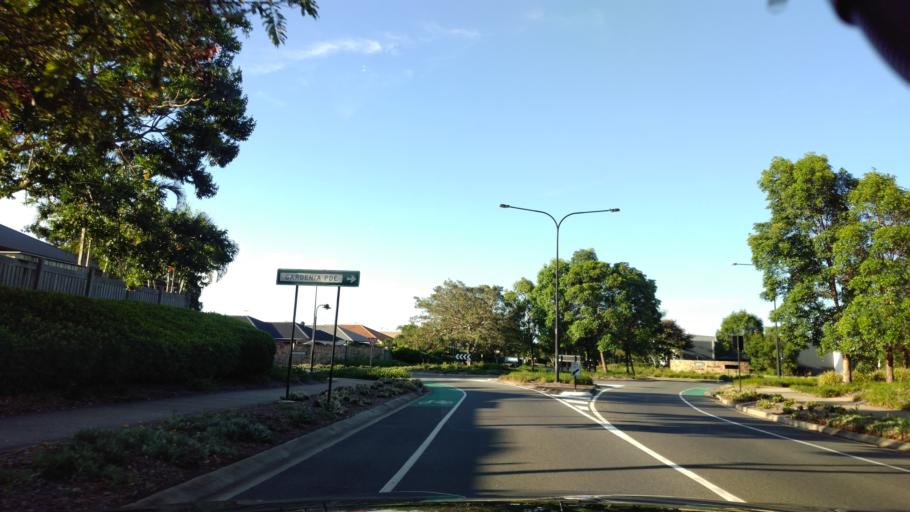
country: AU
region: Queensland
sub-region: Moreton Bay
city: Deception Bay
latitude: -27.2172
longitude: 153.0212
